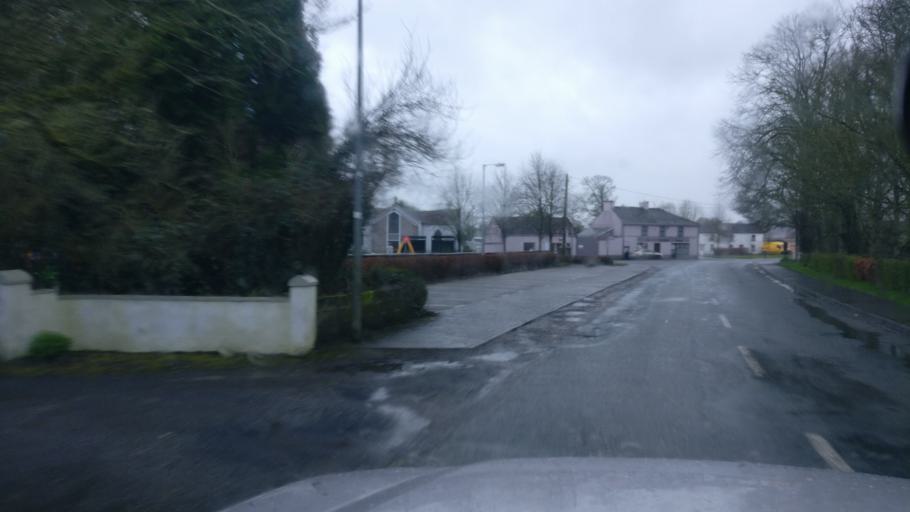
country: IE
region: Connaught
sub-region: County Galway
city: Ballinasloe
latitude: 53.2375
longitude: -8.1738
